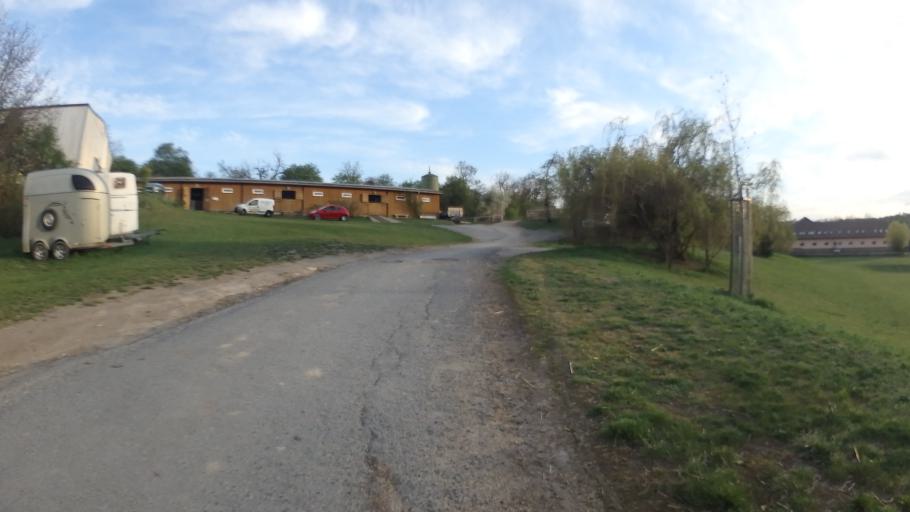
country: CZ
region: South Moravian
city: Moravany
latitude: 49.1435
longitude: 16.5740
